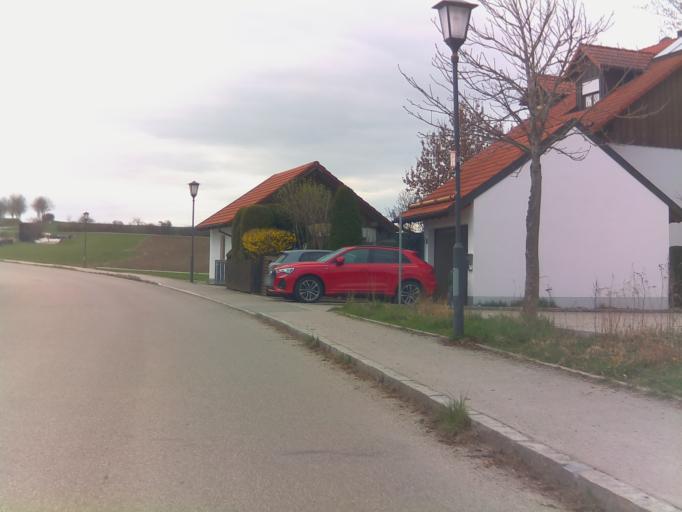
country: DE
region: Bavaria
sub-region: Upper Bavaria
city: Utting am Ammersee
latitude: 48.0232
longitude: 11.0808
